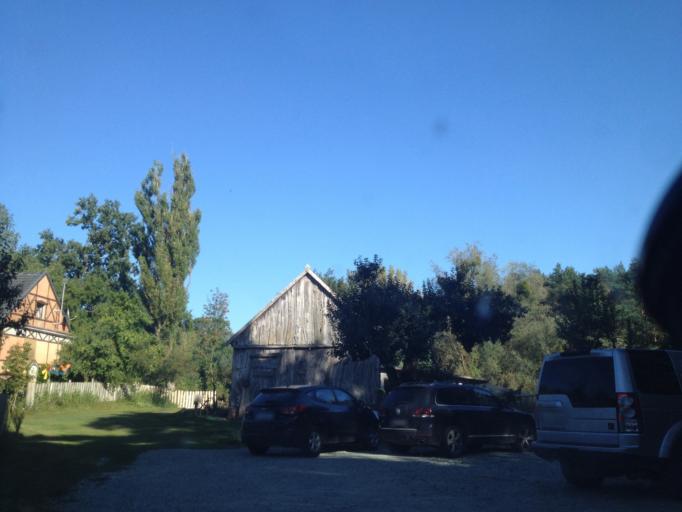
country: PL
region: Greater Poland Voivodeship
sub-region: Powiat sredzki
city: Zaniemysl
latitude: 52.1024
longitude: 17.1356
